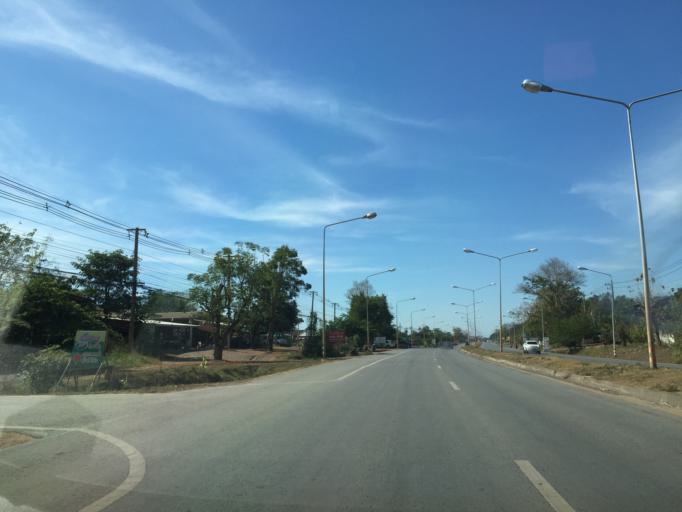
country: TH
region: Changwat Nong Bua Lamphu
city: Na Klang
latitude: 17.3045
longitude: 102.1931
